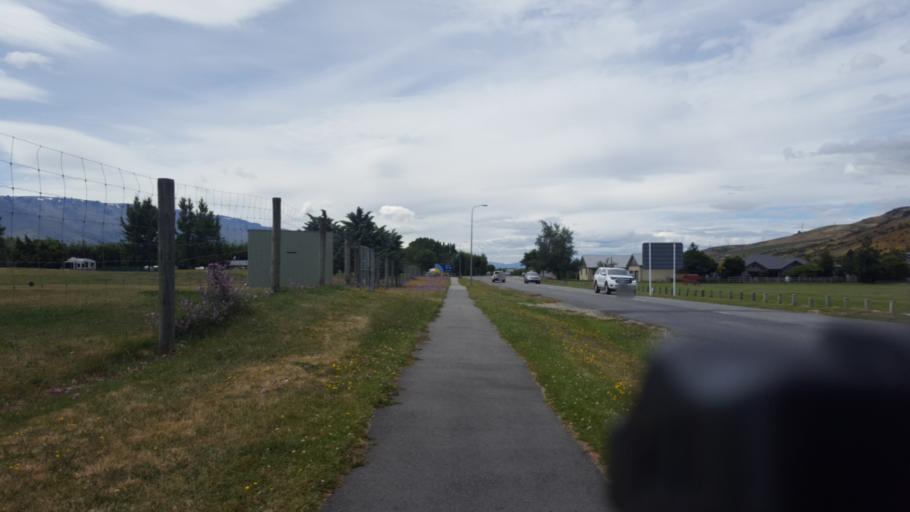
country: NZ
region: Otago
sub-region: Queenstown-Lakes District
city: Wanaka
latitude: -45.0417
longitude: 169.2142
